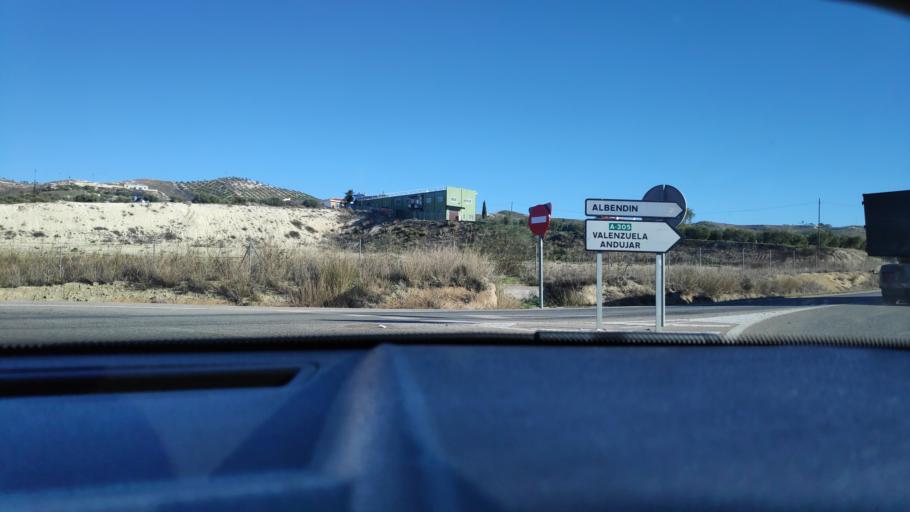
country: ES
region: Andalusia
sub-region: Province of Cordoba
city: Baena
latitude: 37.6231
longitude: -4.3001
